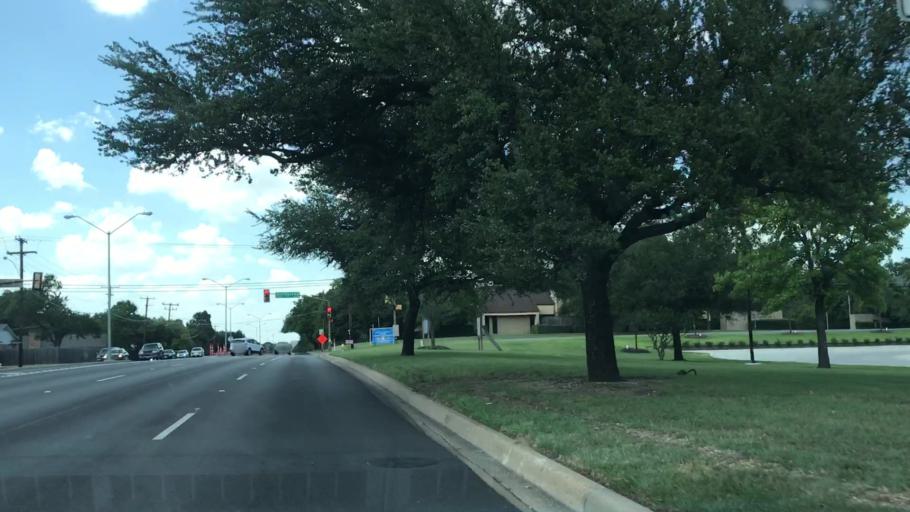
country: US
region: Texas
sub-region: Dallas County
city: Addison
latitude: 32.9015
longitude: -96.8381
